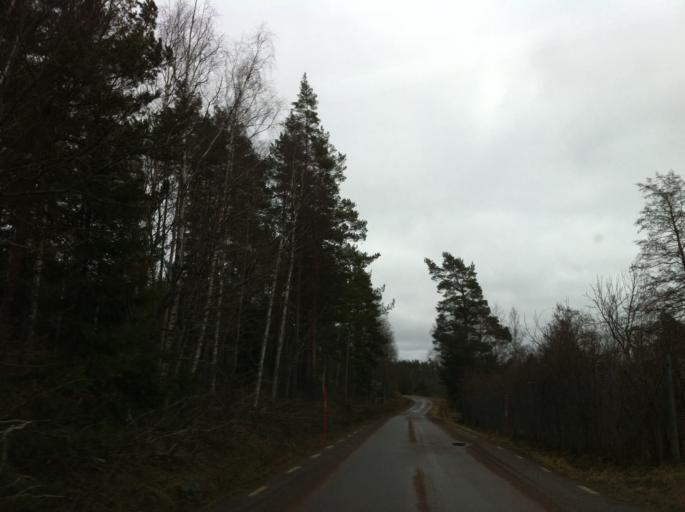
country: SE
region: Kalmar
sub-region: Vasterviks Kommun
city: Forserum
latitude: 57.9256
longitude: 16.5497
